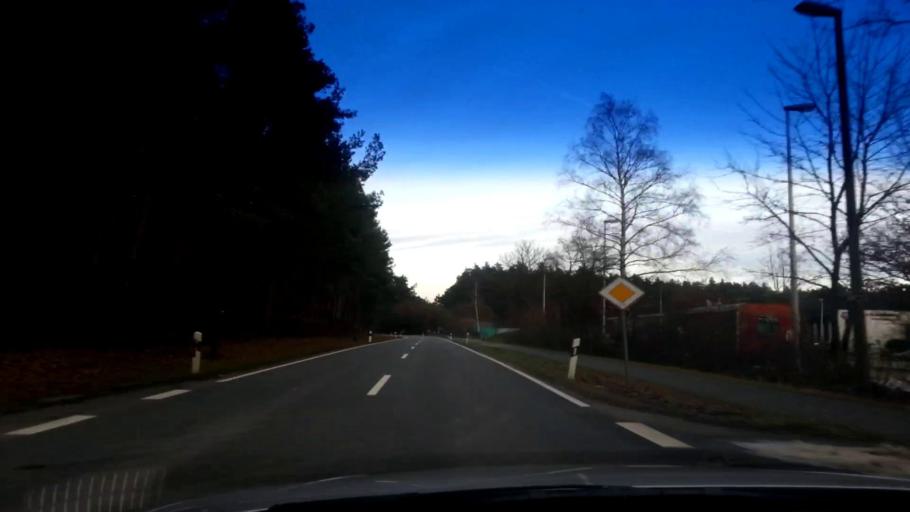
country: DE
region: Bavaria
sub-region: Upper Franconia
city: Strullendorf
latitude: 49.8535
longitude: 10.9712
